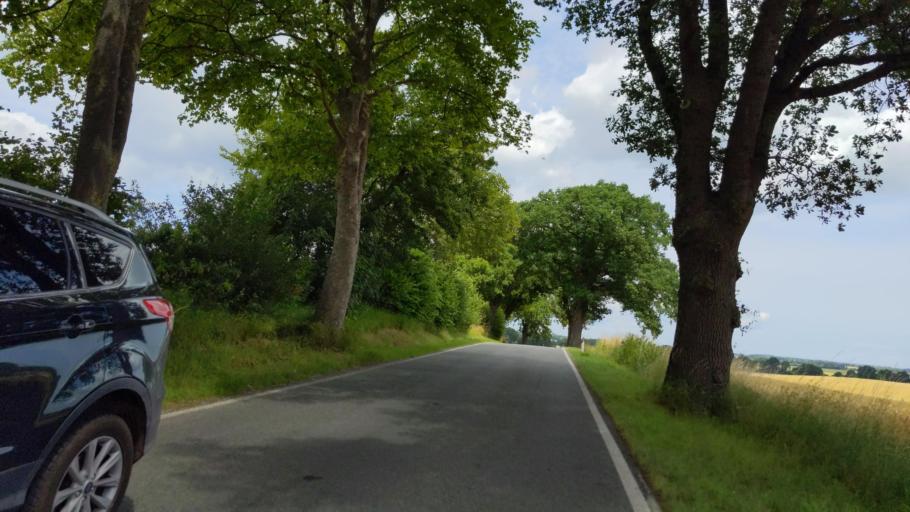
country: DE
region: Mecklenburg-Vorpommern
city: Dassow
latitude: 53.9362
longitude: 10.9707
